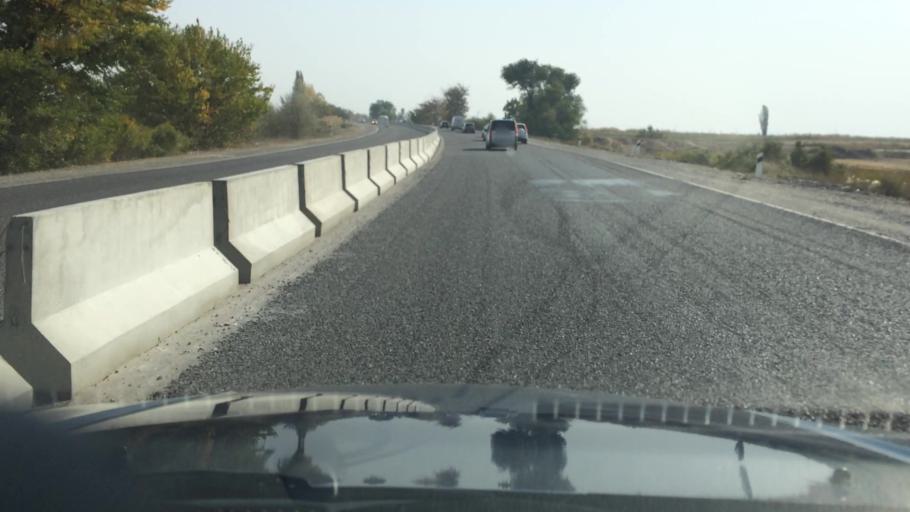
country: KG
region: Chuy
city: Kant
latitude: 42.9592
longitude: 74.9243
